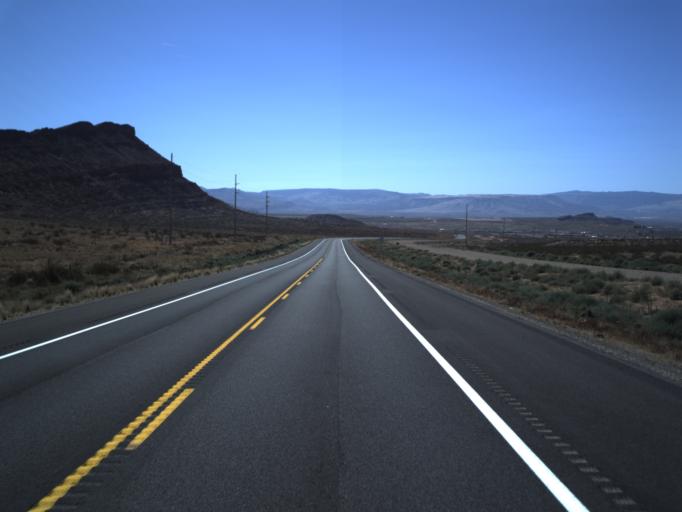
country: US
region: Utah
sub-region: Washington County
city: Washington
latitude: 37.0966
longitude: -113.4686
